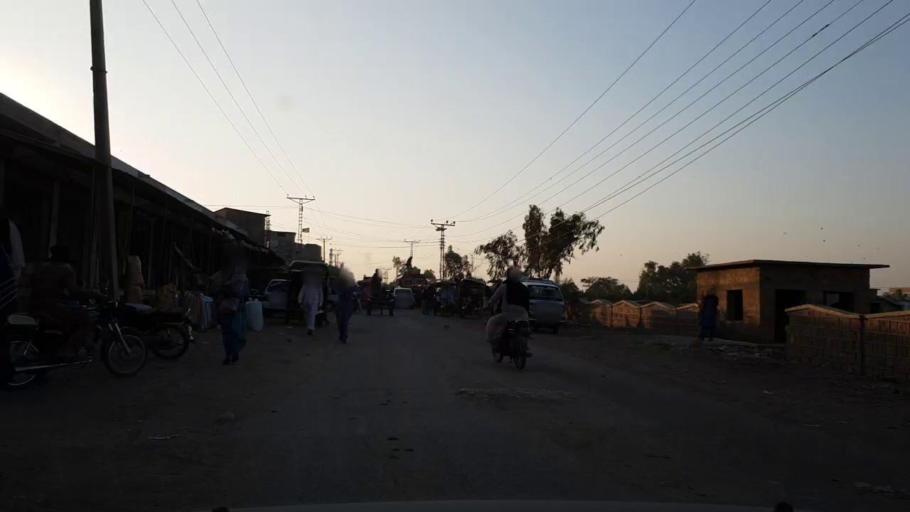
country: PK
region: Sindh
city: Thatta
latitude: 24.6069
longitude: 68.0780
